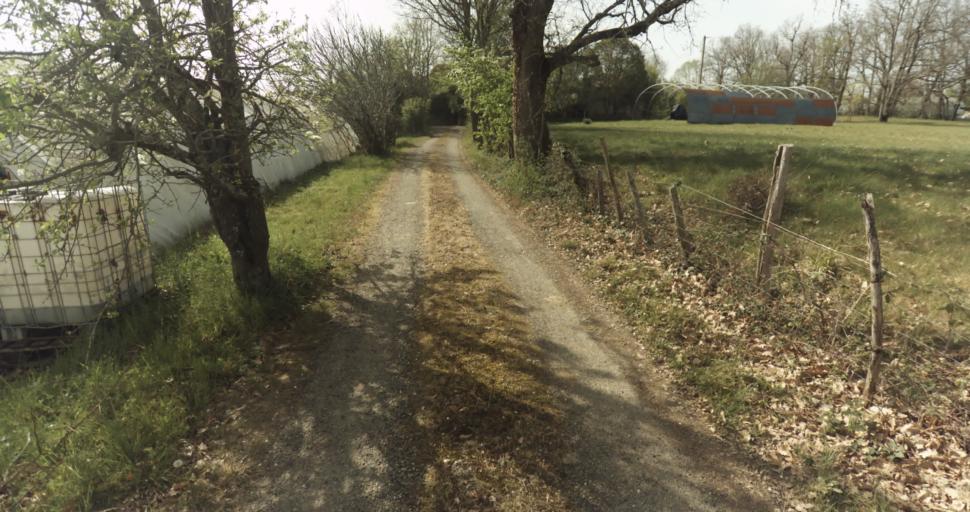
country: FR
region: Midi-Pyrenees
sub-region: Departement du Tarn-et-Garonne
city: Lafrancaise
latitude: 44.1360
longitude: 1.1672
